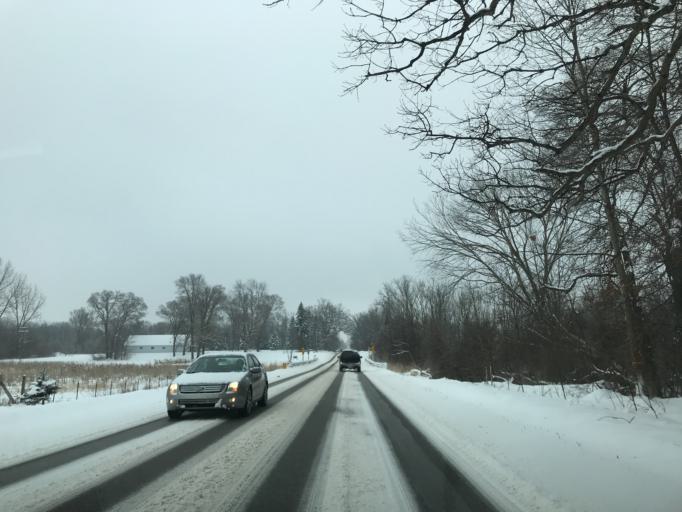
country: US
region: Michigan
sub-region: Oakland County
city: South Lyon
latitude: 42.4204
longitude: -83.6469
